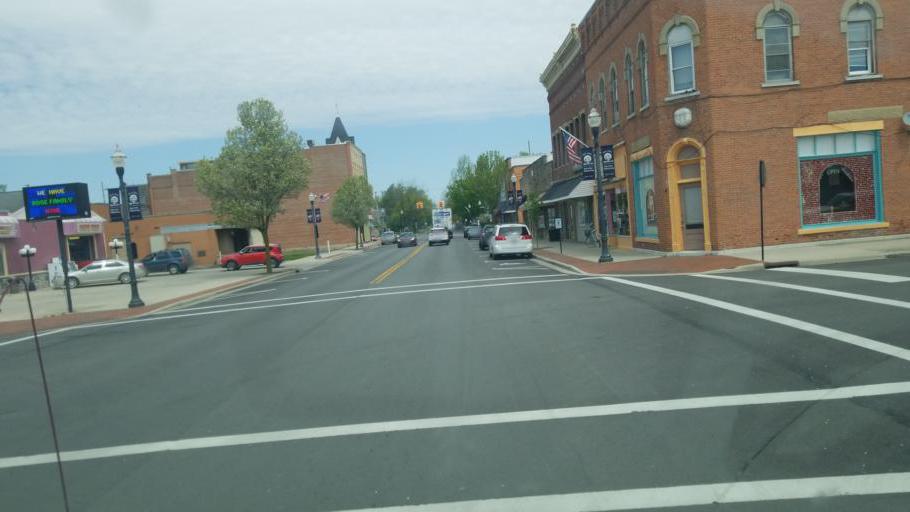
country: US
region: Ohio
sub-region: Hardin County
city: Ada
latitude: 40.7713
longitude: -83.8231
